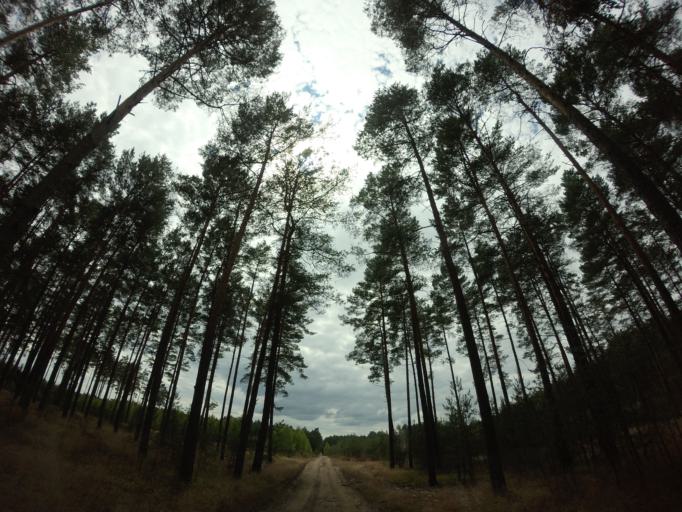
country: PL
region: West Pomeranian Voivodeship
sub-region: Powiat choszczenski
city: Drawno
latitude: 53.1597
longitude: 15.7734
